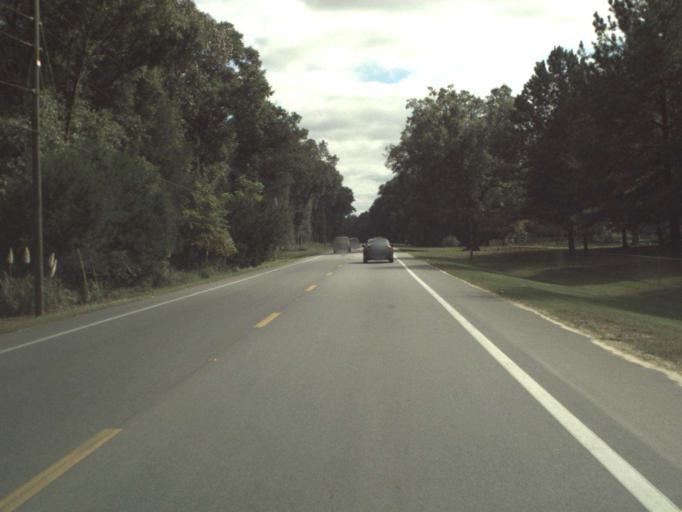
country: US
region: Florida
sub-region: Jackson County
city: Marianna
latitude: 30.6368
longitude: -85.1577
